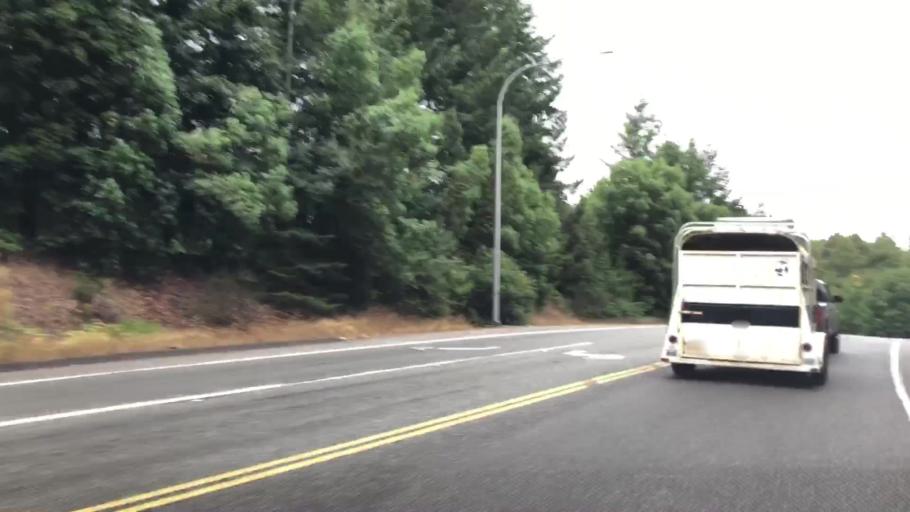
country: US
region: Washington
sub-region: Kitsap County
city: Navy Yard City
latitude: 47.5290
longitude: -122.7038
